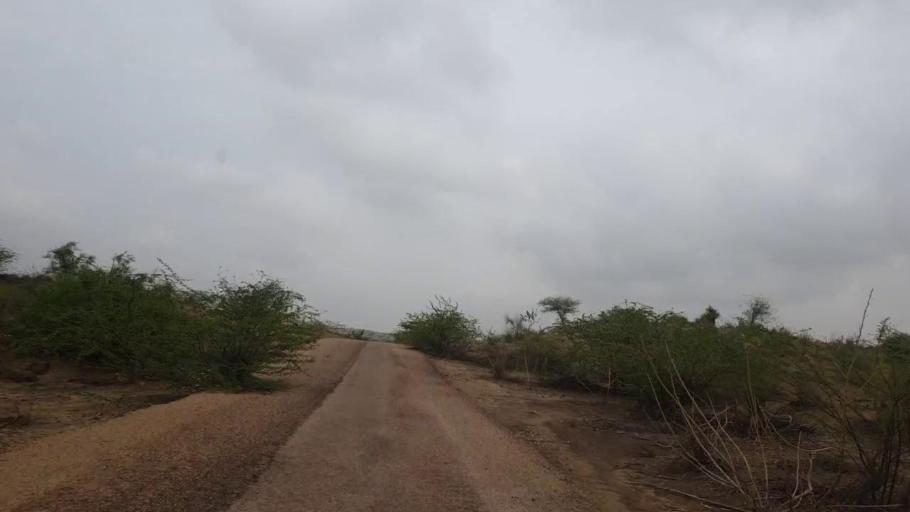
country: PK
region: Sindh
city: Diplo
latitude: 24.5179
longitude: 69.4714
